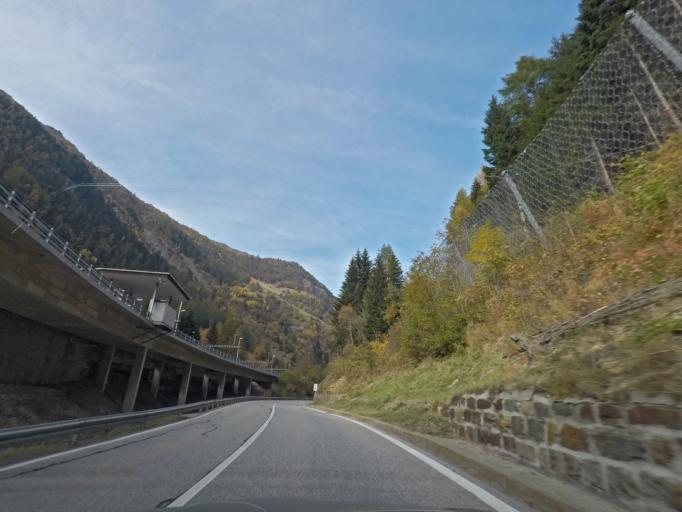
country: CH
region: Valais
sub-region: Leuk District
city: Gampel
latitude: 46.3662
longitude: 7.7565
